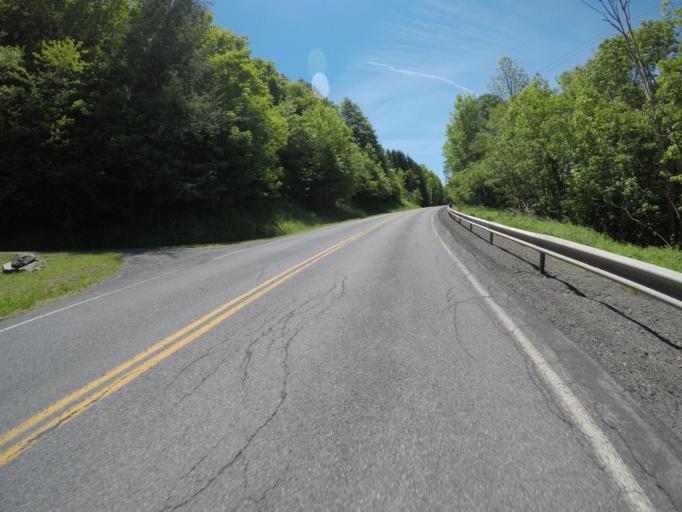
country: US
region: New York
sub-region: Delaware County
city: Delhi
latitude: 42.1923
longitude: -74.8069
